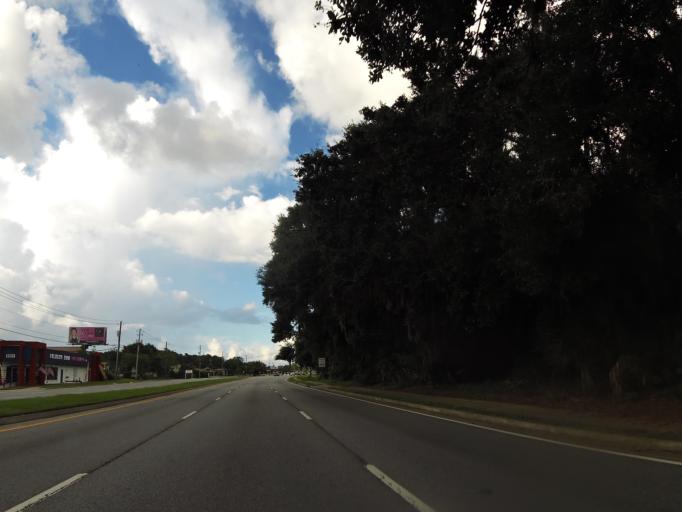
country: US
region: Georgia
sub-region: Glynn County
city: Brunswick
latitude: 31.1749
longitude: -81.4737
